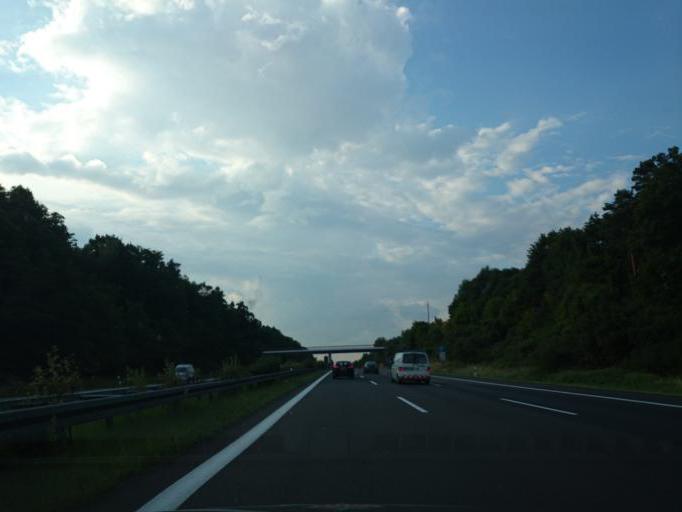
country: DE
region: Brandenburg
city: Grunheide
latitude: 52.4483
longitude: 13.8007
